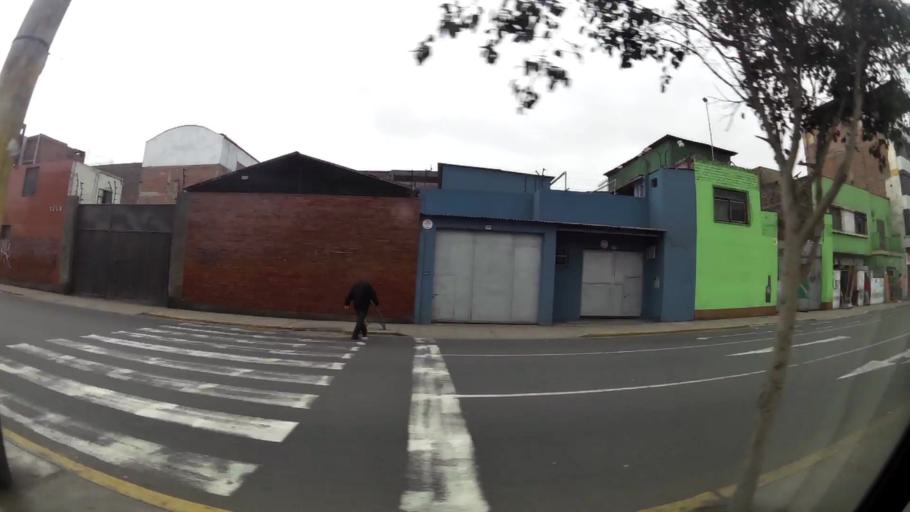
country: PE
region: Lima
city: Lima
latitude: -12.0610
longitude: -77.0590
